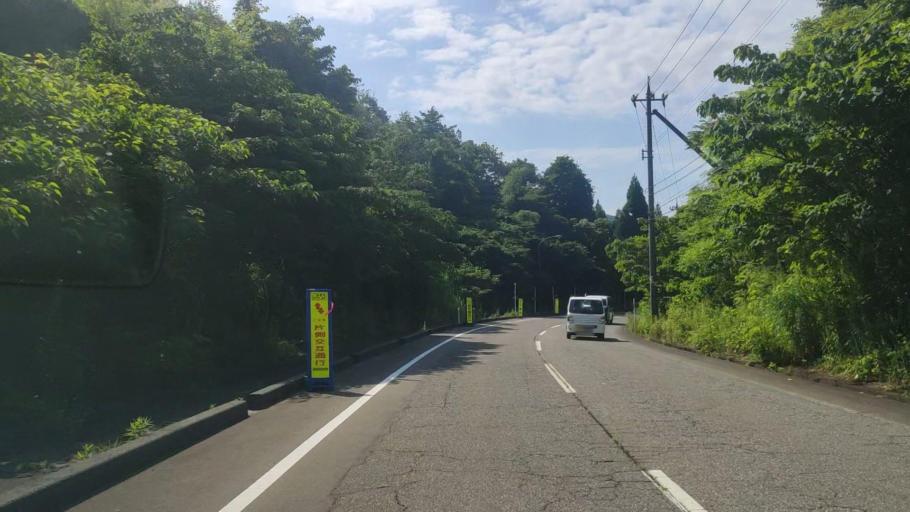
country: JP
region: Ishikawa
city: Komatsu
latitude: 36.3831
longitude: 136.4971
